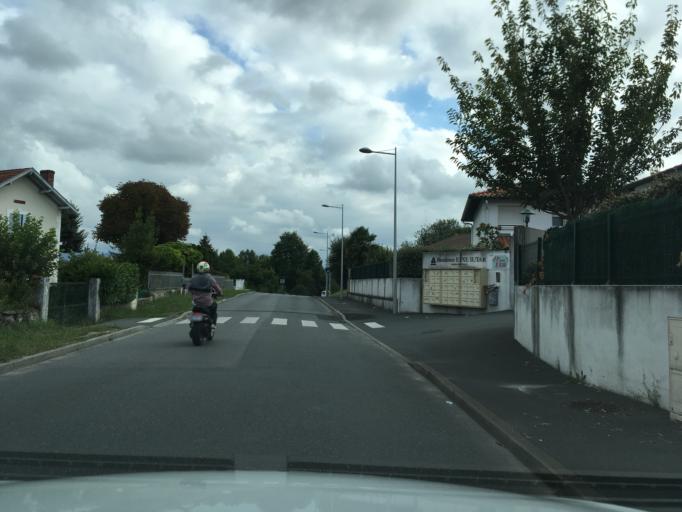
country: FR
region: Aquitaine
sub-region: Departement des Pyrenees-Atlantiques
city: Anglet
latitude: 43.4581
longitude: -1.4969
